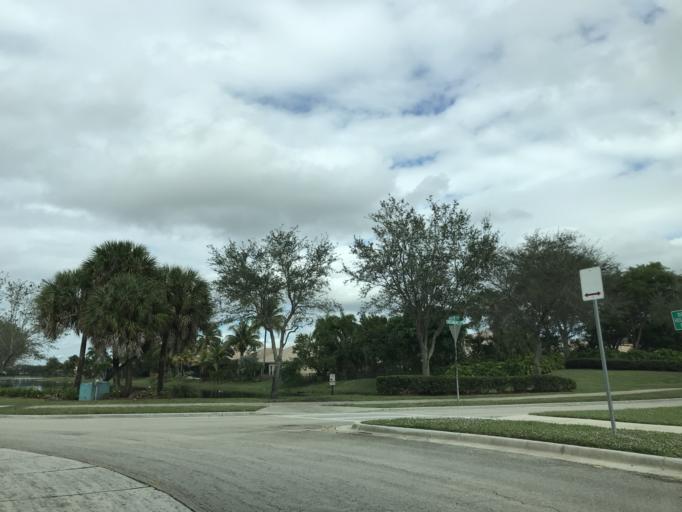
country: US
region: Florida
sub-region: Broward County
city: Coral Springs
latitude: 26.3062
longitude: -80.2752
